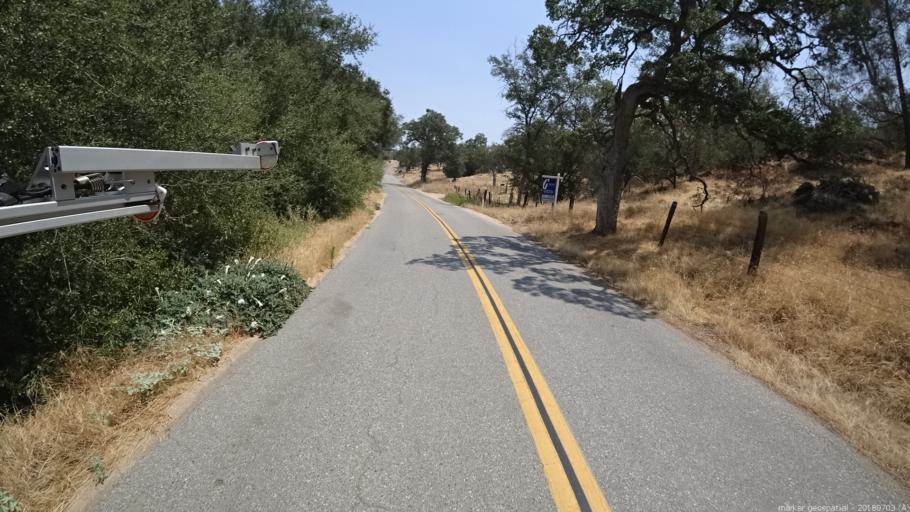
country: US
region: California
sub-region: Madera County
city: Yosemite Lakes
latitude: 37.0602
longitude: -119.6851
